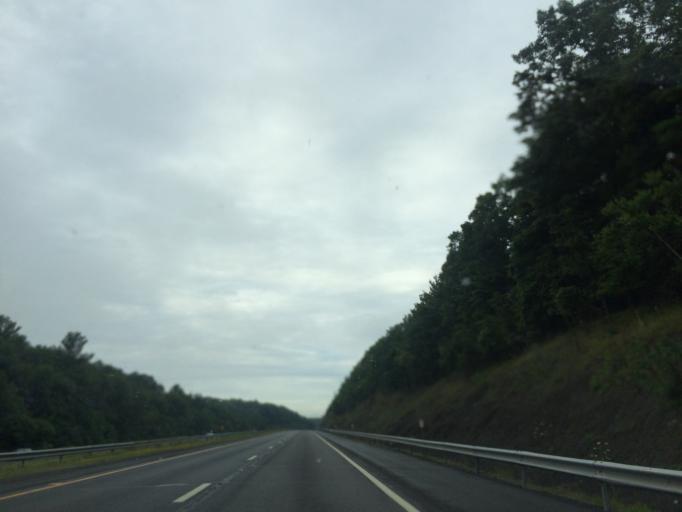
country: US
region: New York
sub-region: Greene County
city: Coxsackie
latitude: 42.3201
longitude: -73.8661
